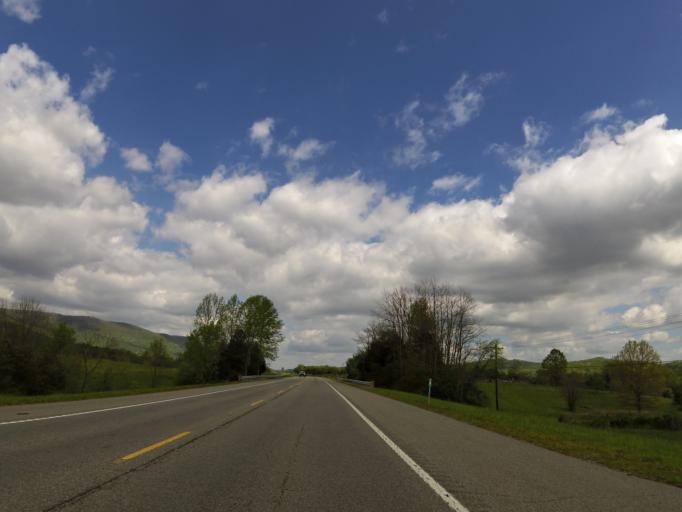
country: US
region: Tennessee
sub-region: Campbell County
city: Fincastle
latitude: 36.4473
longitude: -83.9368
